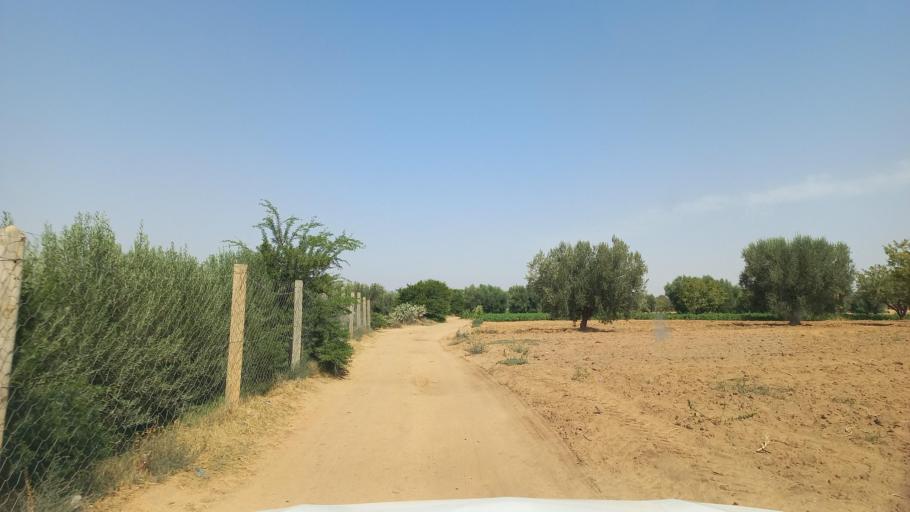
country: TN
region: Al Qasrayn
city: Kasserine
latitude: 35.2514
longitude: 9.0478
